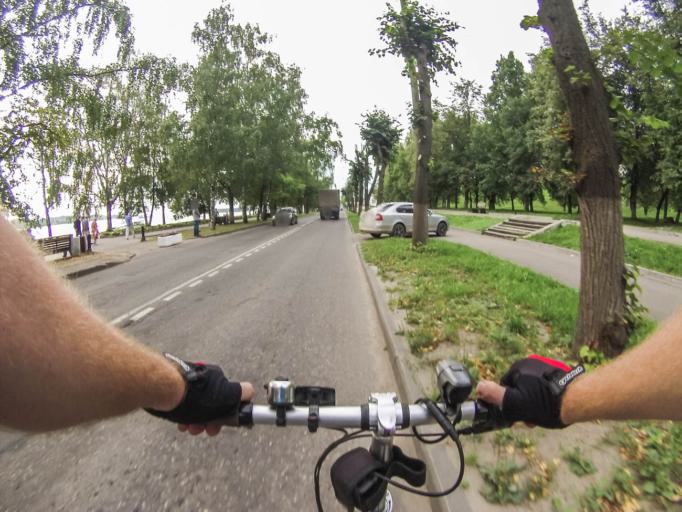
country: RU
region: Kostroma
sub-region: Kostromskoy Rayon
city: Kostroma
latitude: 57.7620
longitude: 40.9277
